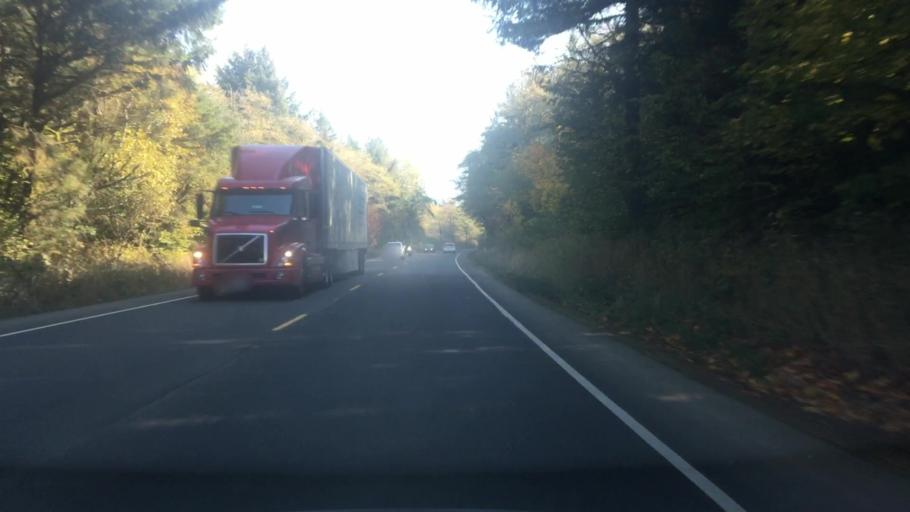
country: US
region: Oregon
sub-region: Lincoln County
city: Rose Lodge
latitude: 45.0119
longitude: -123.9264
